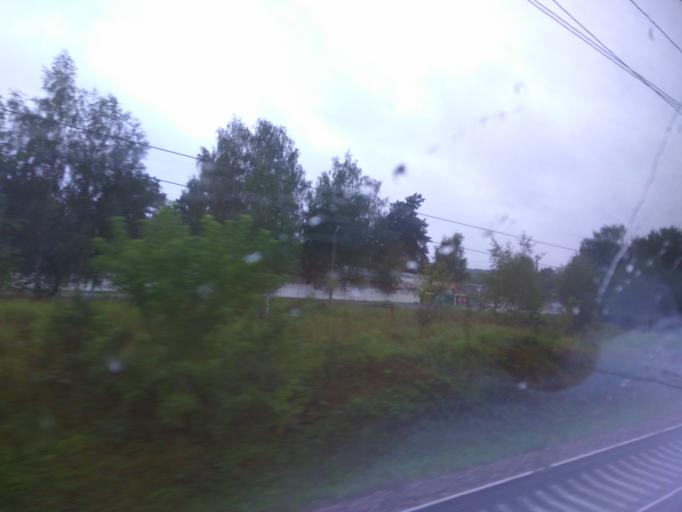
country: RU
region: Moskovskaya
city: Kashira
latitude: 54.8710
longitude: 38.1236
